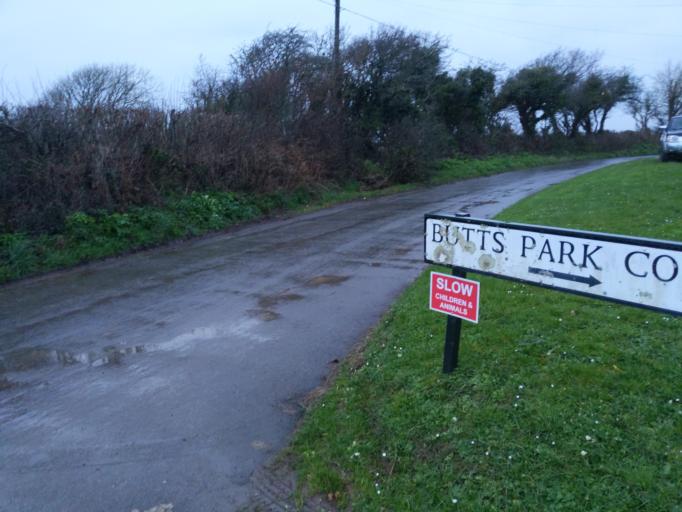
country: GB
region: England
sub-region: Devon
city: Yealmpton
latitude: 50.3225
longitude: -4.0321
